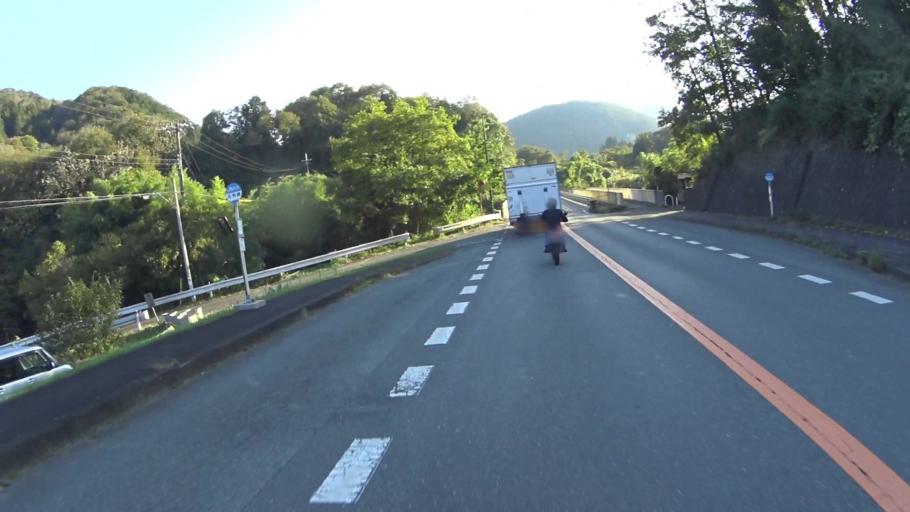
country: JP
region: Kyoto
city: Ayabe
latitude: 35.2062
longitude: 135.2471
